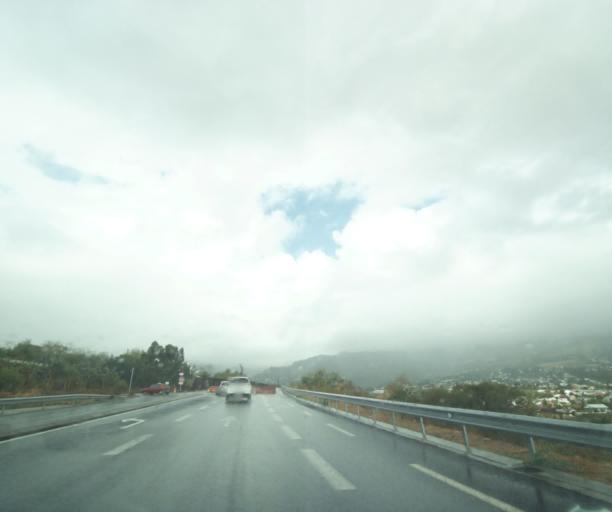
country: RE
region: Reunion
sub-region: Reunion
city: Le Port
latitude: -20.9735
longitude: 55.3171
